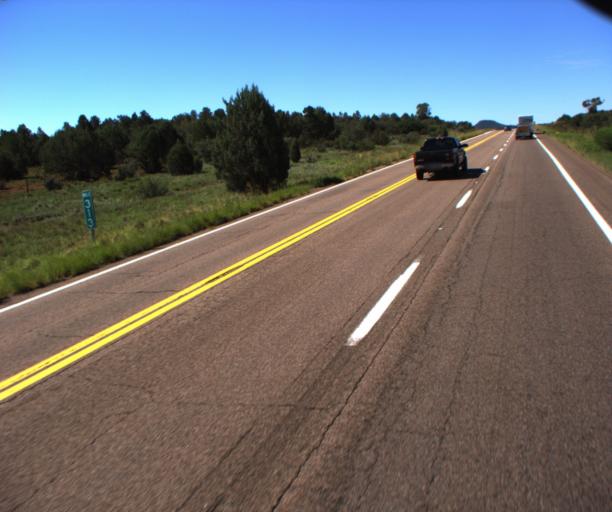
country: US
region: Arizona
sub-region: Navajo County
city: Cibecue
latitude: 33.9711
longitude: -110.3171
